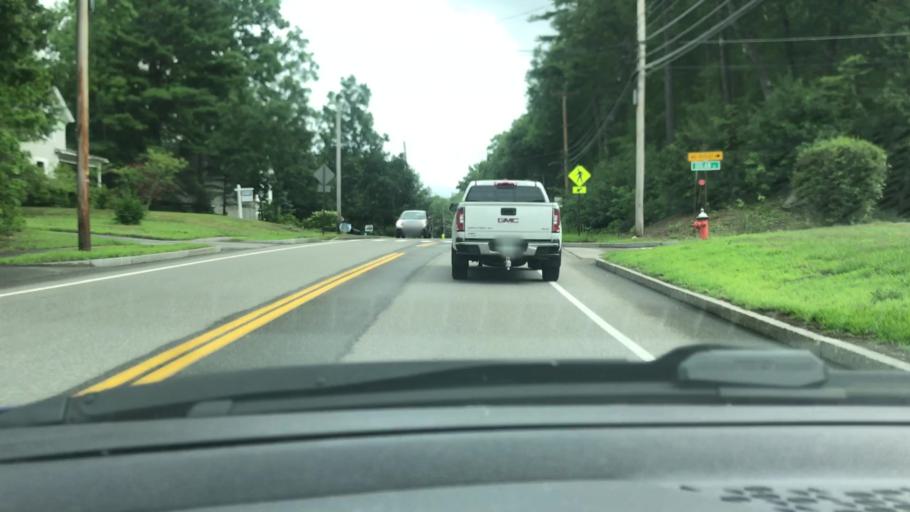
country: US
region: New Hampshire
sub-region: Merrimack County
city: East Concord
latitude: 43.2355
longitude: -71.5635
